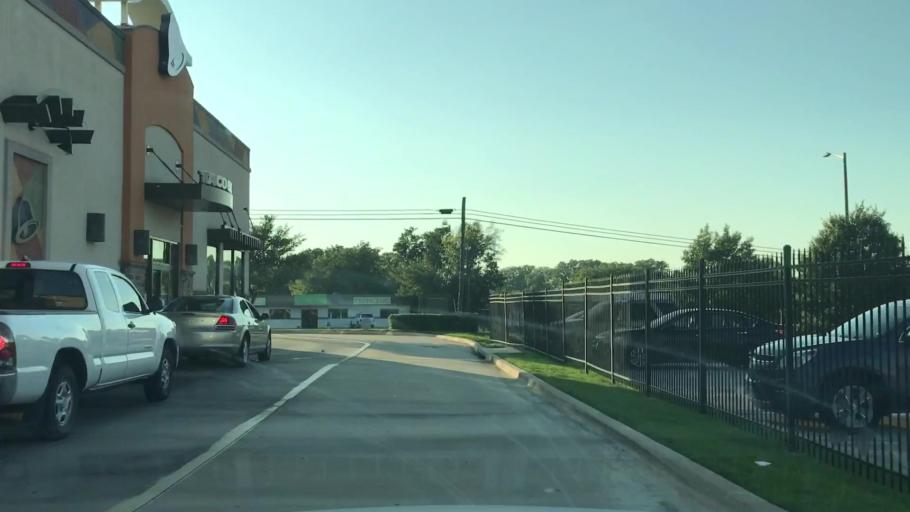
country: US
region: Texas
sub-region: Denton County
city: Denton
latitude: 33.1990
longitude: -97.1372
